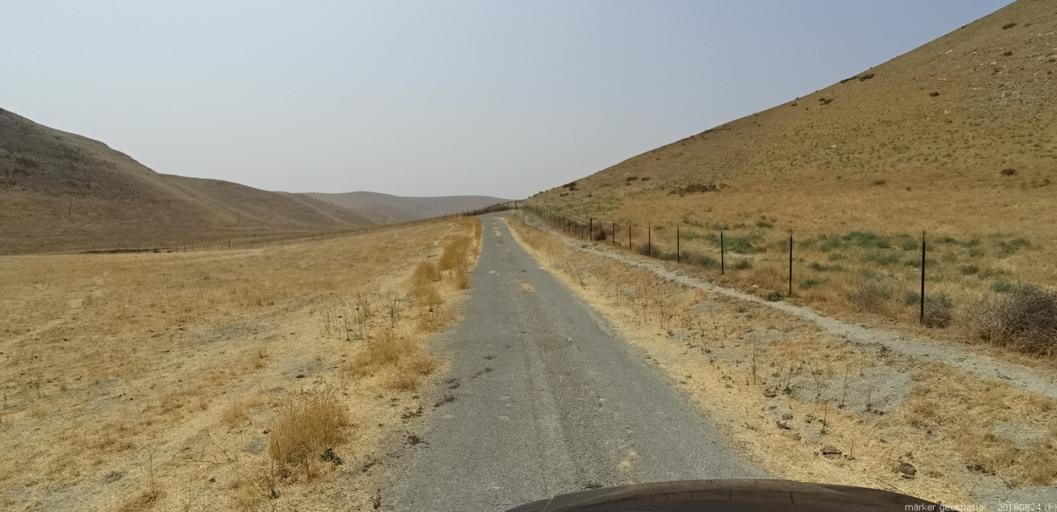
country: US
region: California
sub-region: Monterey County
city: King City
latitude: 36.1993
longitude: -120.9482
